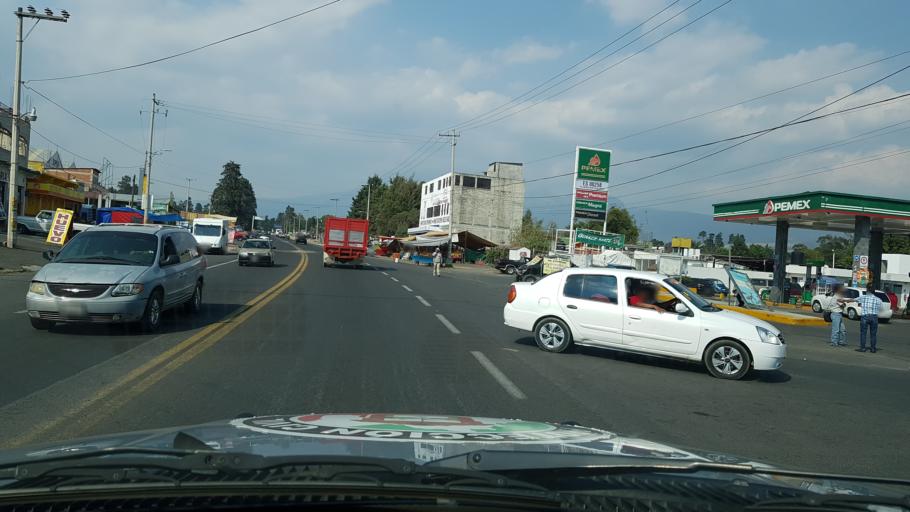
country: MX
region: Mexico
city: Ozumba de Alzate
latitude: 19.0468
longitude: -98.7942
